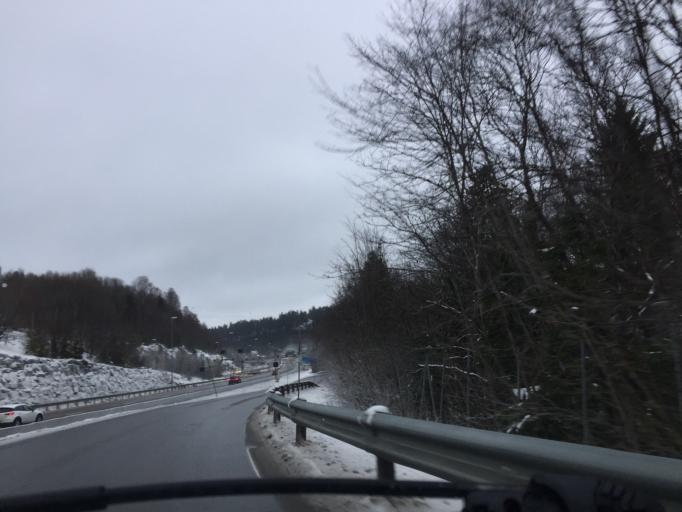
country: NO
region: Akershus
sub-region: As
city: As
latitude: 59.7023
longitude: 10.7381
